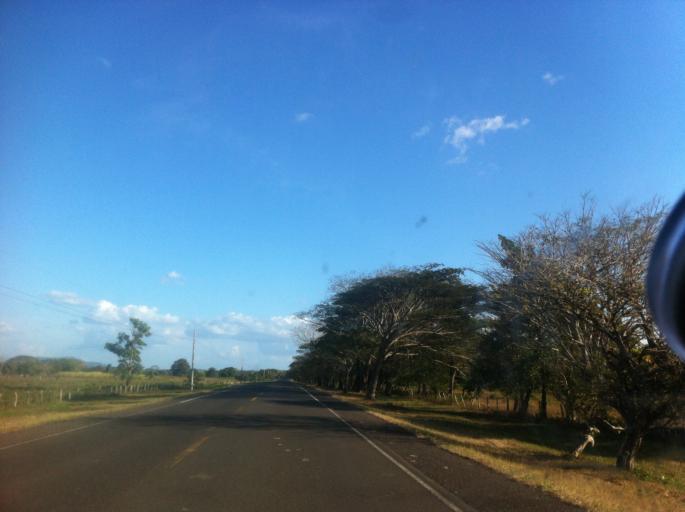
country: NI
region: Rio San Juan
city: Morrito
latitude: 11.7686
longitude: -85.0107
